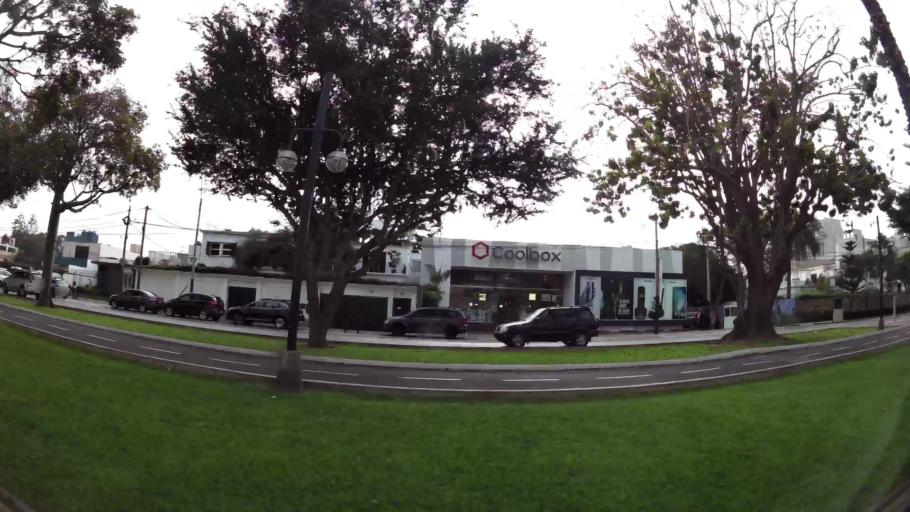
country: PE
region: Lima
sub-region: Lima
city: San Isidro
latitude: -12.1002
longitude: -77.0568
